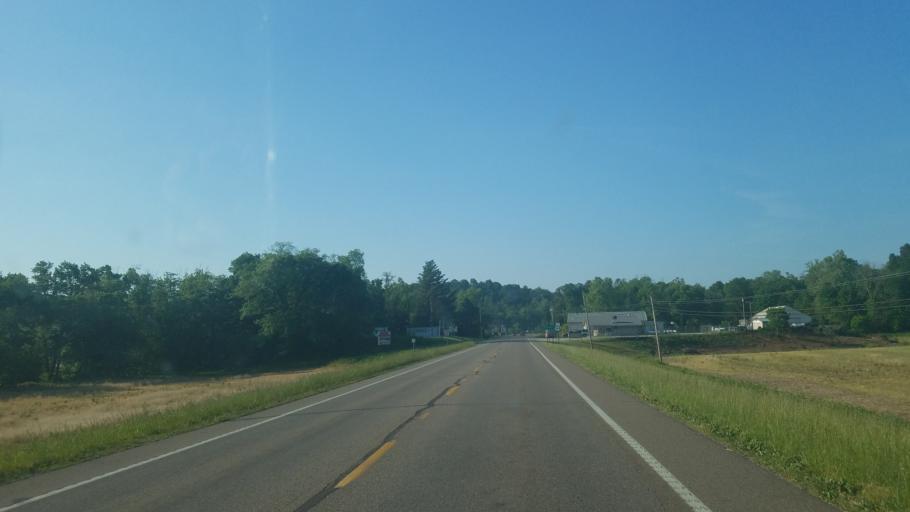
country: US
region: West Virginia
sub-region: Mason County
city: New Haven
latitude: 39.0902
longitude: -81.9263
